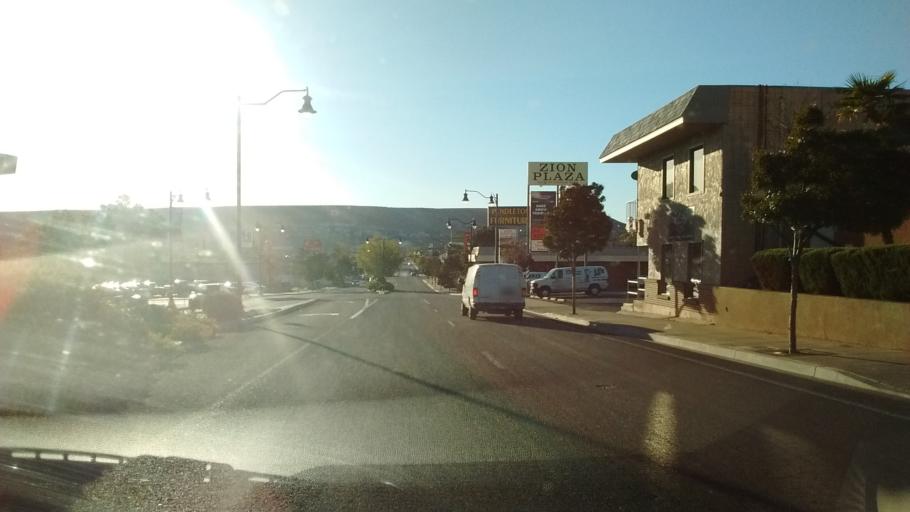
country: US
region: Utah
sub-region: Washington County
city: Saint George
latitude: 37.1099
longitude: -113.5721
